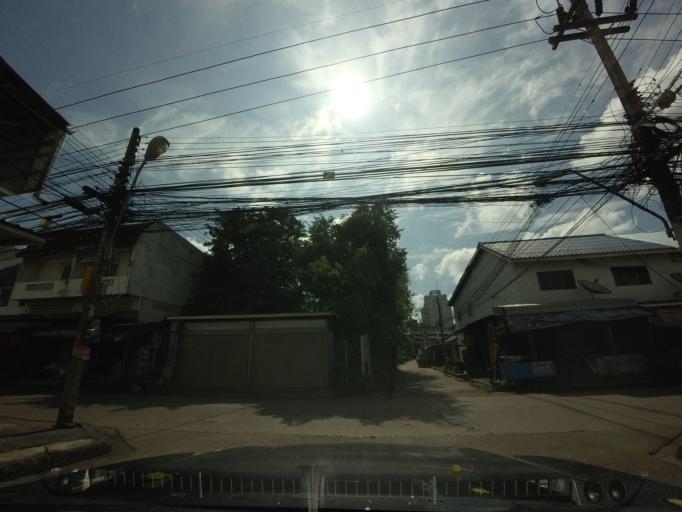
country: TH
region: Changwat Udon Thani
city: Udon Thani
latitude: 17.3988
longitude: 102.8011
